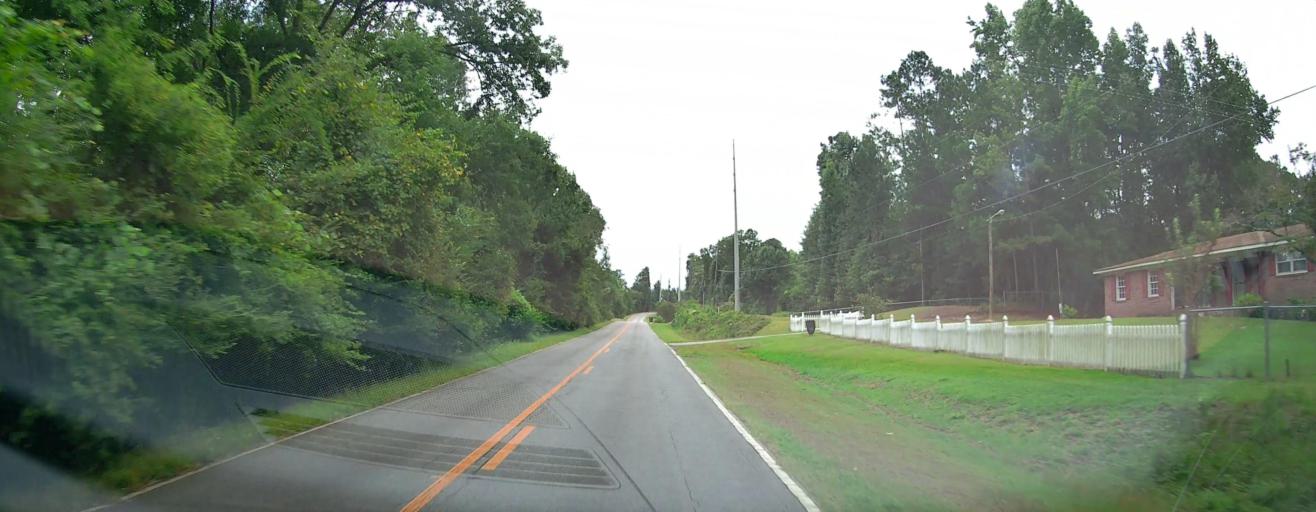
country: US
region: Georgia
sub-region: Bibb County
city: Macon
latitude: 32.7993
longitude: -83.5308
